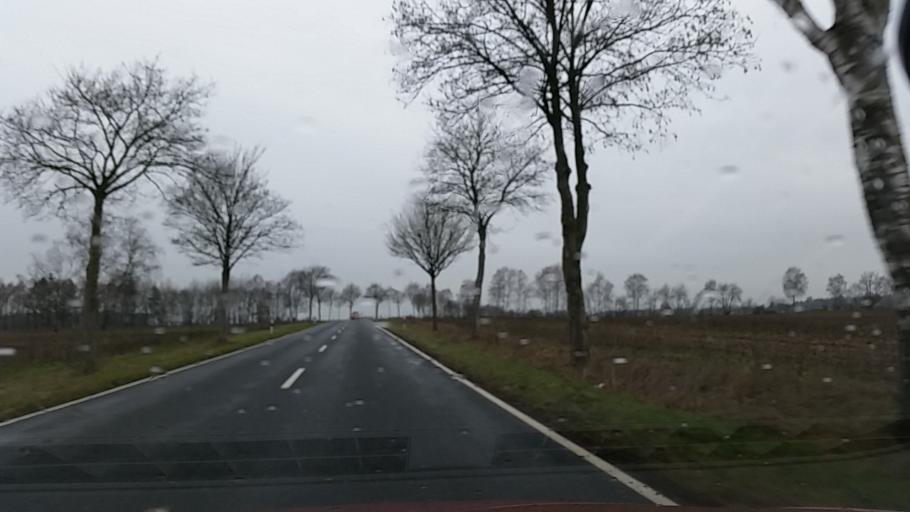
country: DE
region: Lower Saxony
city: Sprakensehl
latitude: 52.7672
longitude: 10.4779
